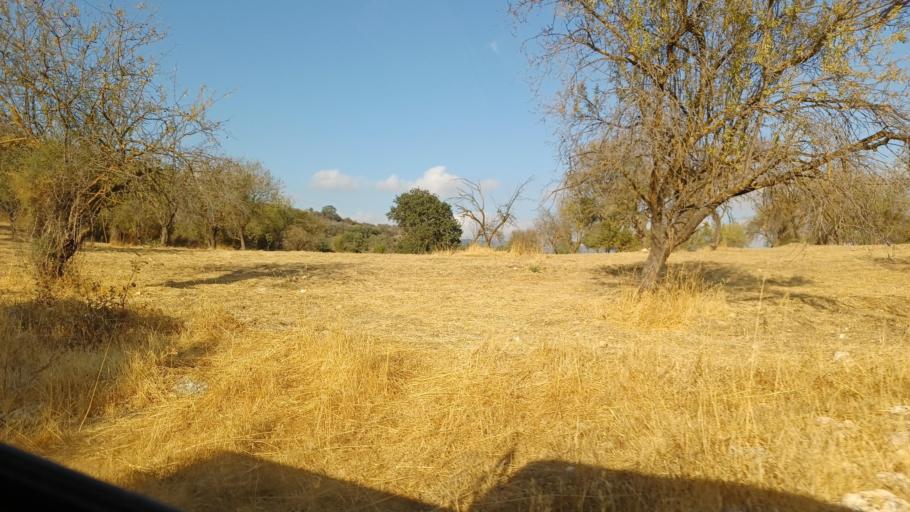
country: CY
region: Pafos
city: Tala
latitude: 34.9267
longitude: 32.4948
